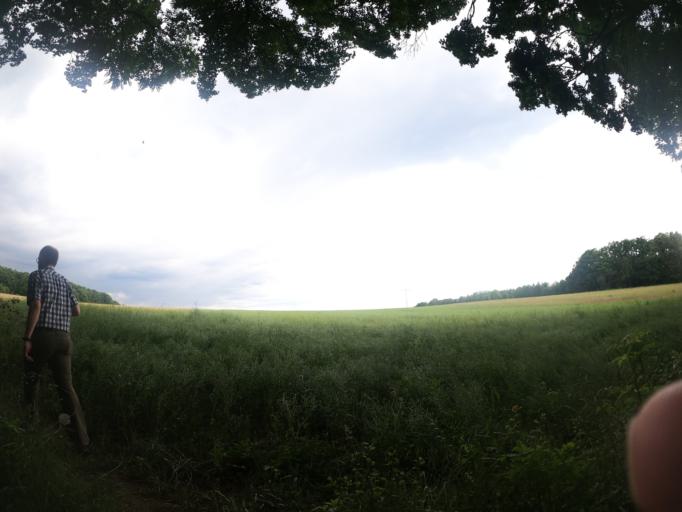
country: DE
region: Bavaria
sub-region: Upper Franconia
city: Memmelsdorf
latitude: 49.9365
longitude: 10.9747
